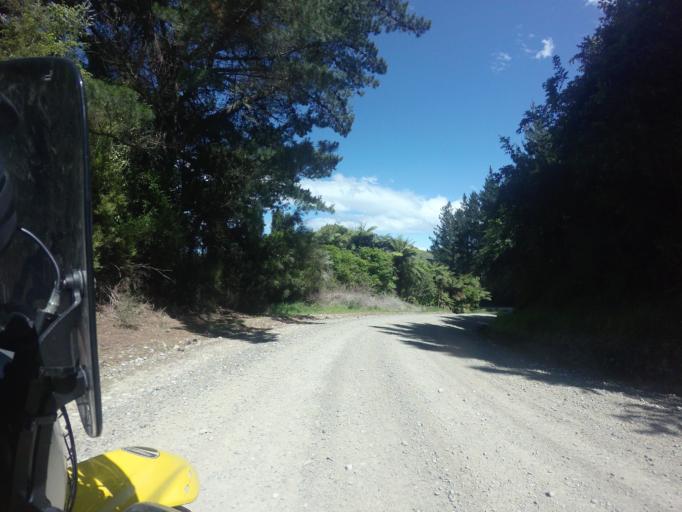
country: NZ
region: Hawke's Bay
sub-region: Wairoa District
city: Wairoa
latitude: -38.9818
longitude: 177.7030
